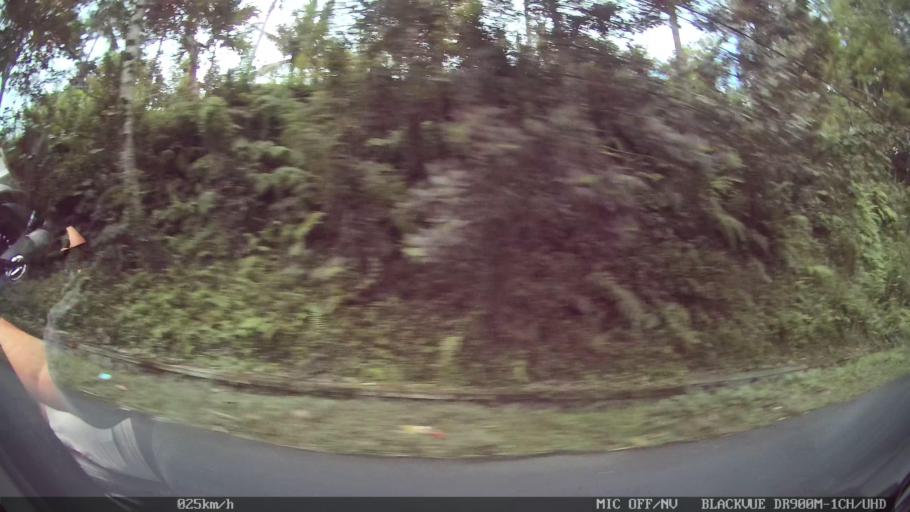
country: ID
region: Bali
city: Bangli
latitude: -8.4500
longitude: 115.3452
